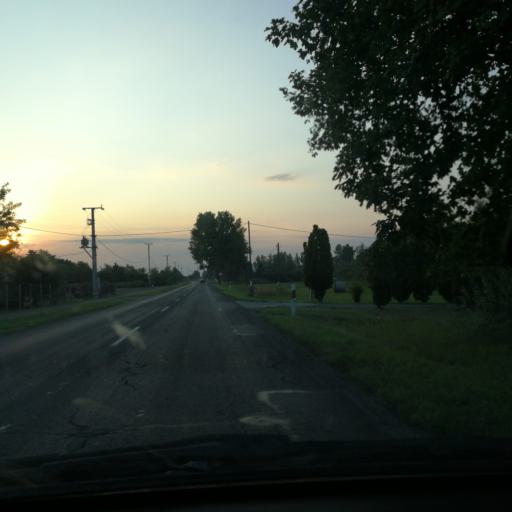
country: HU
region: Bacs-Kiskun
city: Soltvadkert
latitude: 46.5872
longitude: 19.3473
